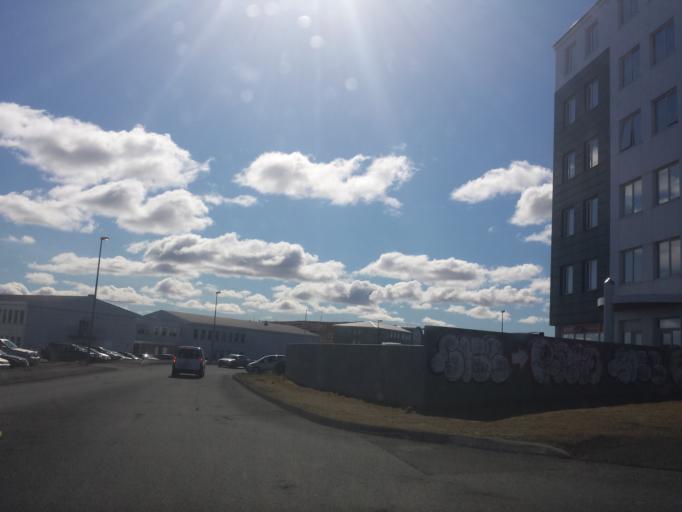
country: IS
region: Capital Region
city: Kopavogur
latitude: 64.0978
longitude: -21.8914
